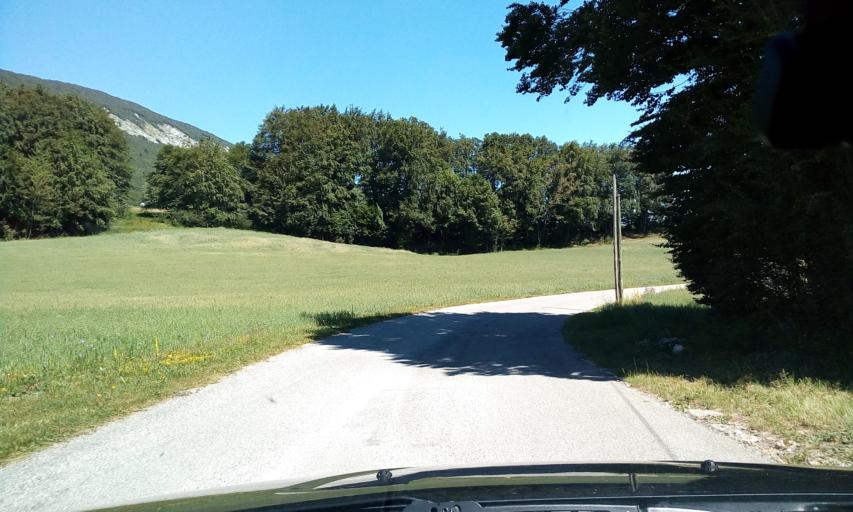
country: FR
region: Rhone-Alpes
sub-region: Departement de la Drome
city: Die
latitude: 44.8679
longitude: 5.3577
